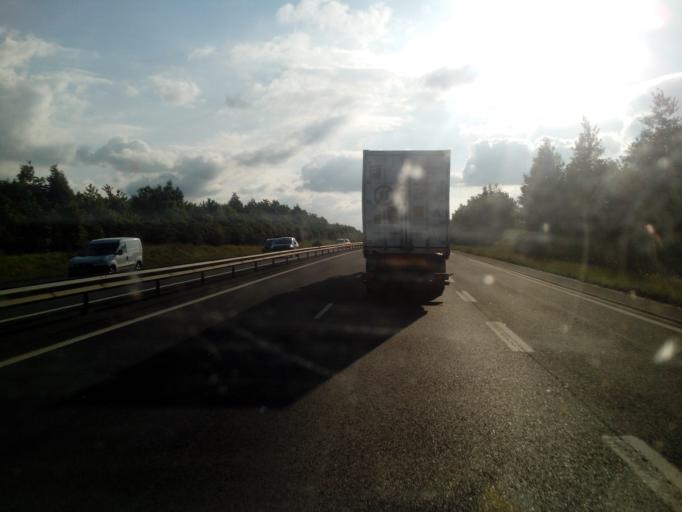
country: FR
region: Lower Normandy
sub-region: Departement du Calvados
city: Cahagnes
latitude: 49.0505
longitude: -0.7174
